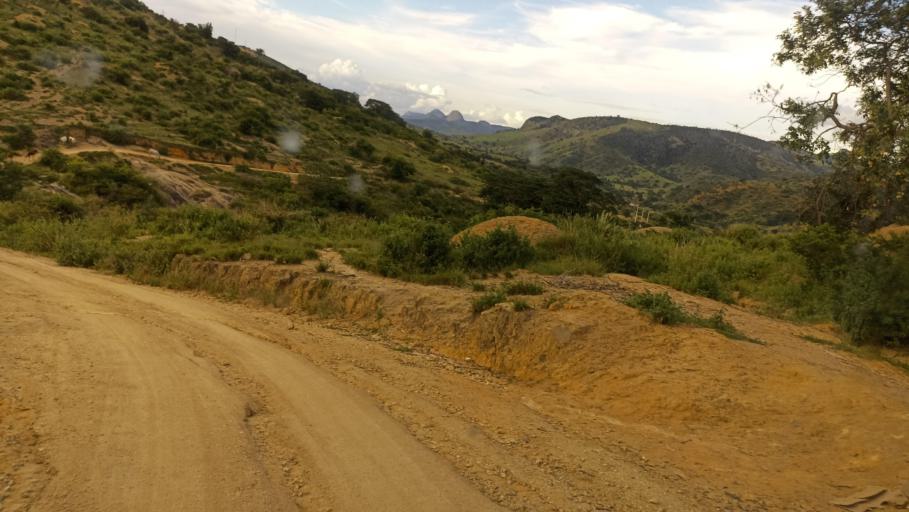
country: BR
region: Minas Gerais
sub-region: Almenara
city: Almenara
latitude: -16.5408
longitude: -40.4453
